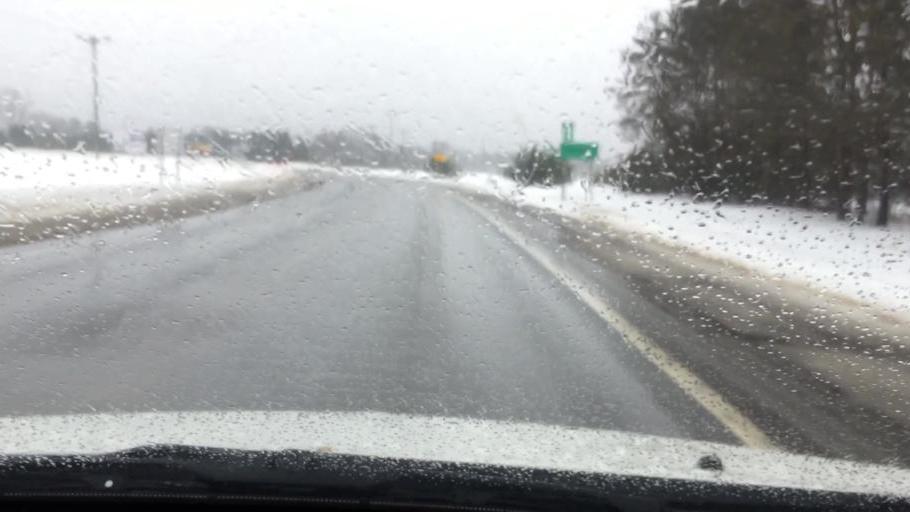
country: US
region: Michigan
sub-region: Antrim County
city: Mancelona
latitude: 44.9132
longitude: -85.0510
